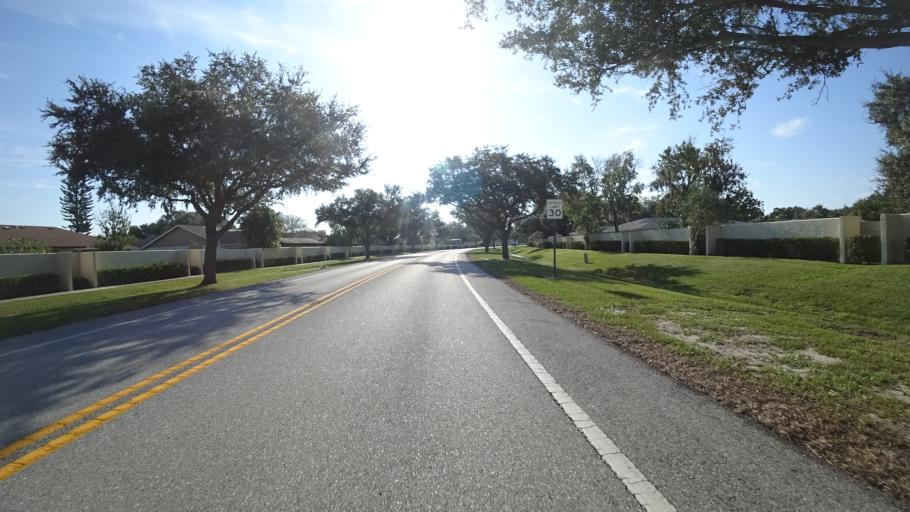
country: US
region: Florida
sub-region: Sarasota County
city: Desoto Lakes
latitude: 27.4185
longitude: -82.4937
